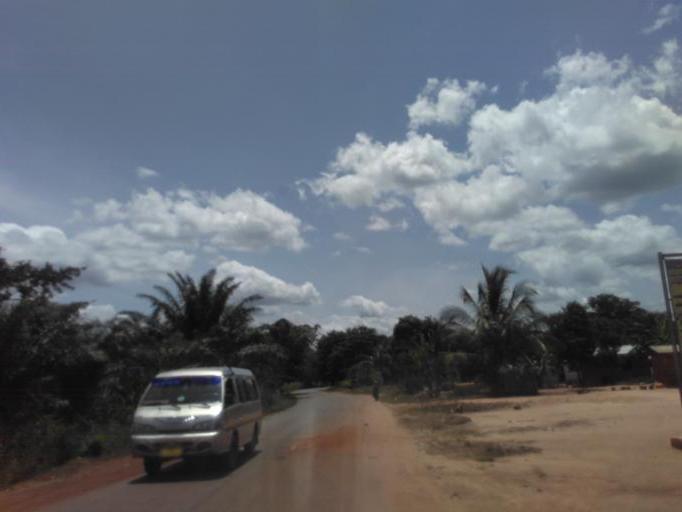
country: GH
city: Akropong
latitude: 6.0954
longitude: -0.1018
